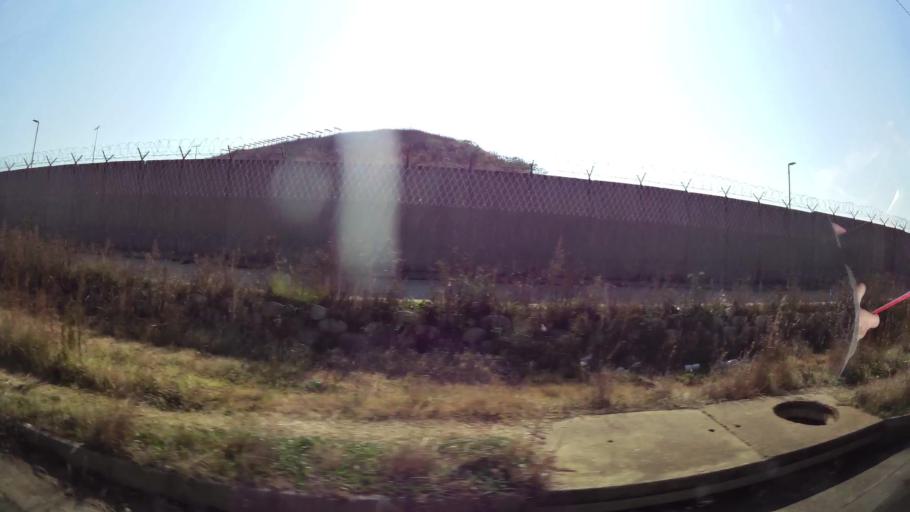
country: ZA
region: Gauteng
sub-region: Ekurhuleni Metropolitan Municipality
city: Boksburg
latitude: -26.1690
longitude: 28.2479
